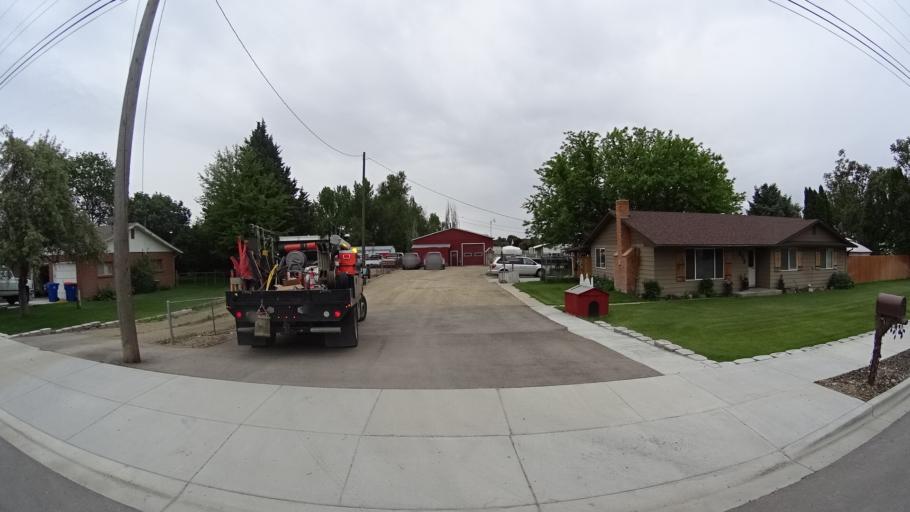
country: US
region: Idaho
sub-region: Ada County
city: Meridian
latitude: 43.6337
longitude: -116.3916
